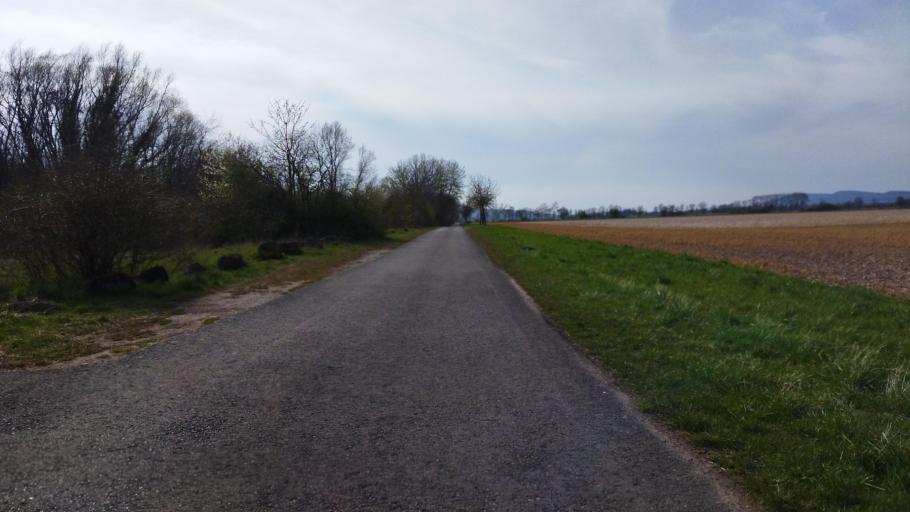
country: DE
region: Lower Saxony
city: Hessisch Oldendorf
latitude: 52.1632
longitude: 9.2334
